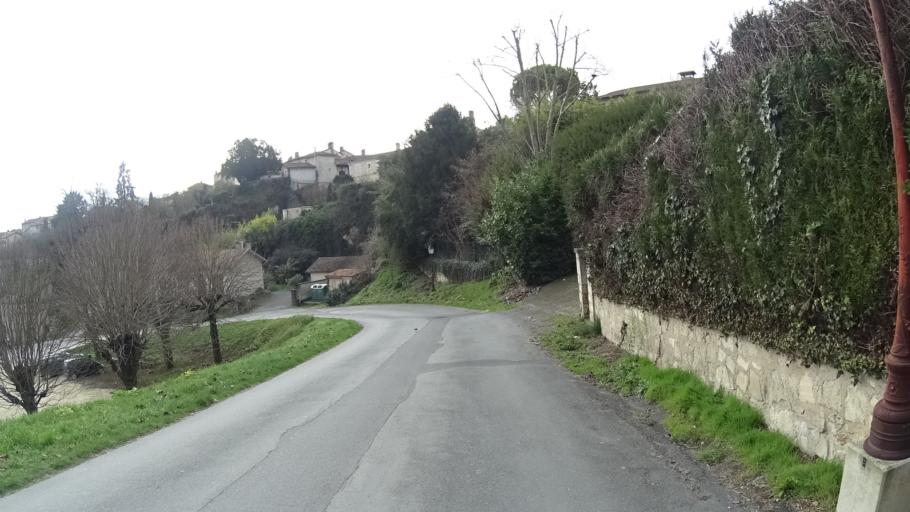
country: FR
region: Aquitaine
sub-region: Departement de la Dordogne
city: Saint-Aulaye
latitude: 45.2725
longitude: 0.1692
